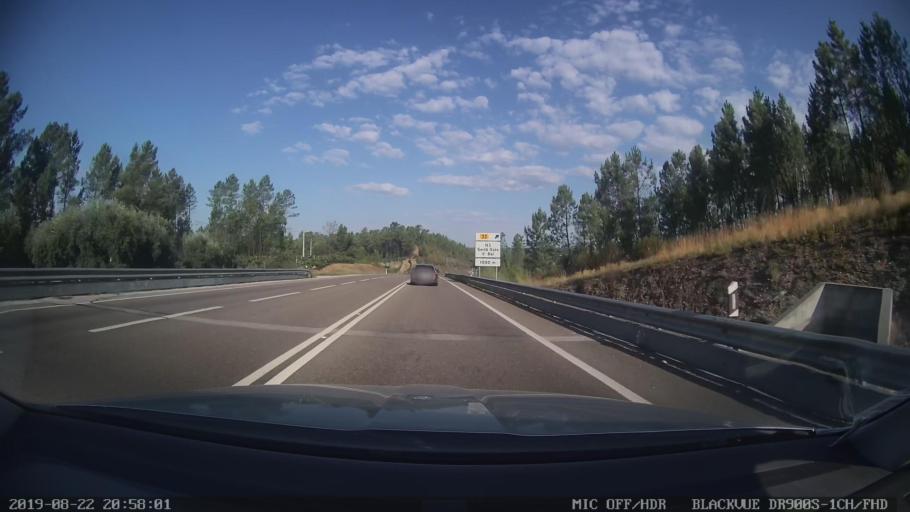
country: PT
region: Castelo Branco
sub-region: Serta
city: Serta
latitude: 39.7972
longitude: -8.0754
